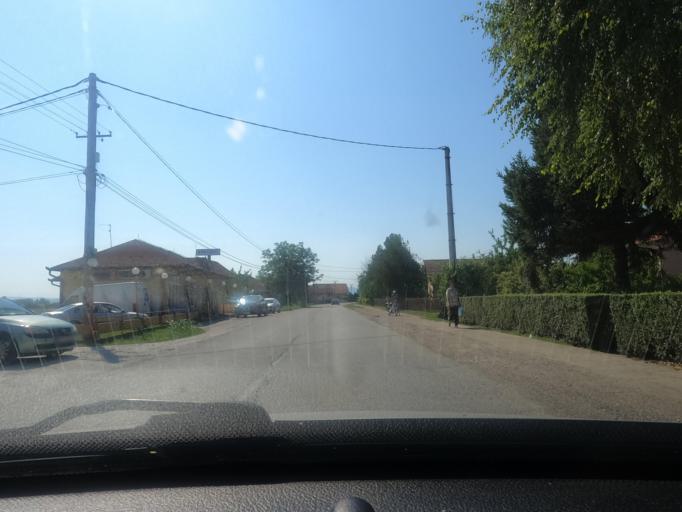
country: RS
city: Lipnicki Sor
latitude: 44.5809
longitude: 19.2619
